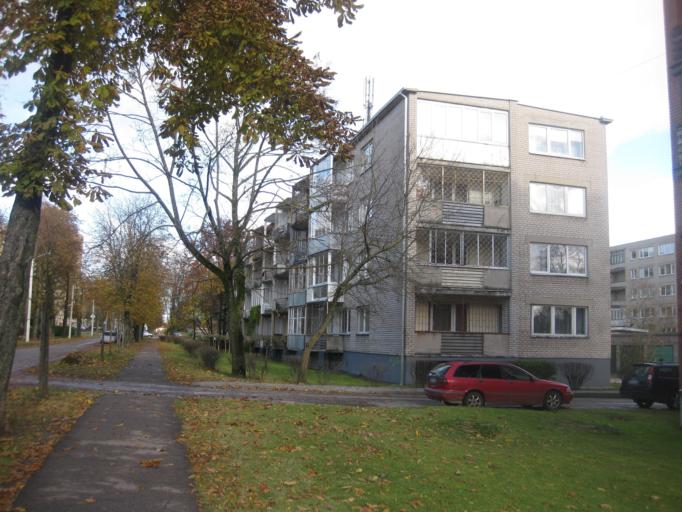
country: LT
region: Kauno apskritis
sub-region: Kaunas
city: Eiguliai
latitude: 54.9063
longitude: 23.9411
